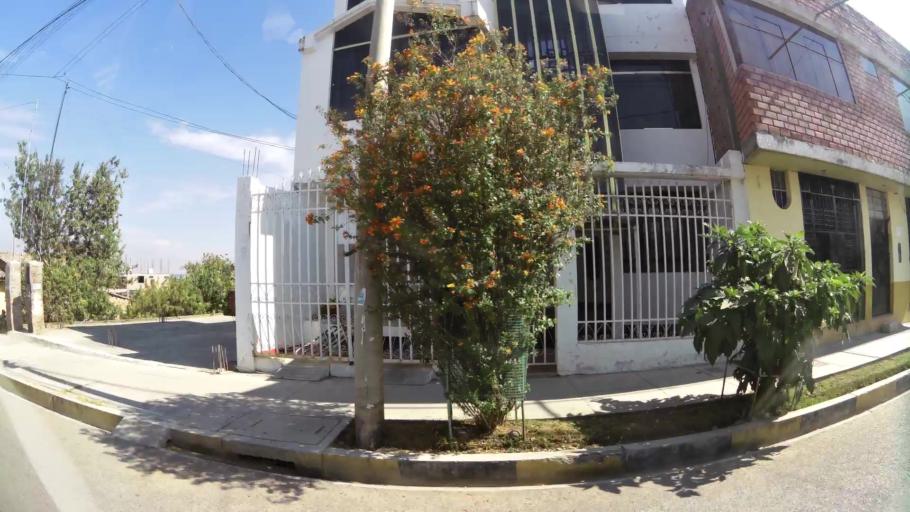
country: PE
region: Junin
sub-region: Provincia de Huancayo
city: El Tambo
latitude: -12.0777
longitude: -75.2248
